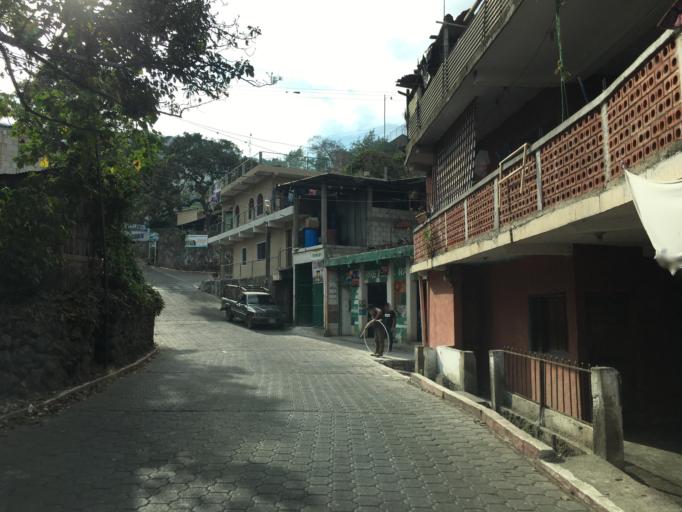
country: GT
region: Solola
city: Santa Catarina Palopo
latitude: 14.6698
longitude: -91.1678
